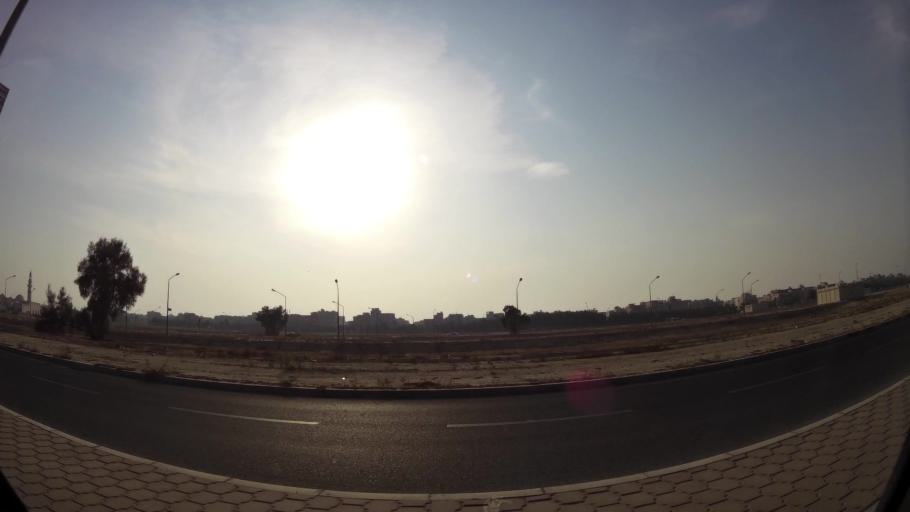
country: KW
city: Al Funaytis
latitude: 29.2401
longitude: 48.0868
